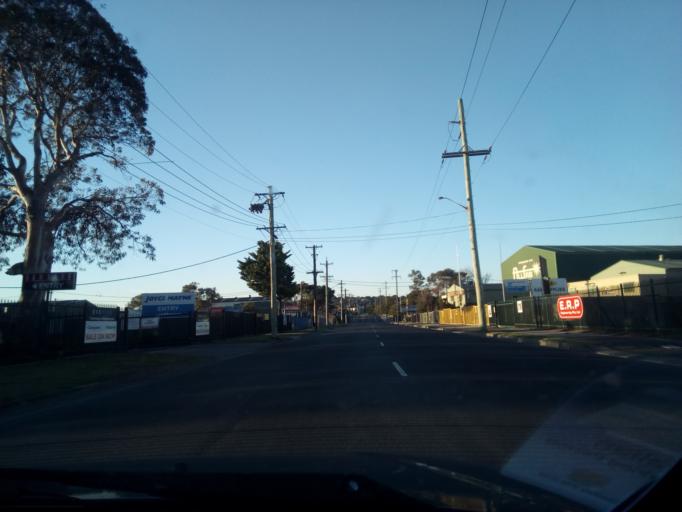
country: AU
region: New South Wales
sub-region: Wollongong
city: Port Kembla
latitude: -34.4944
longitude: 150.8922
